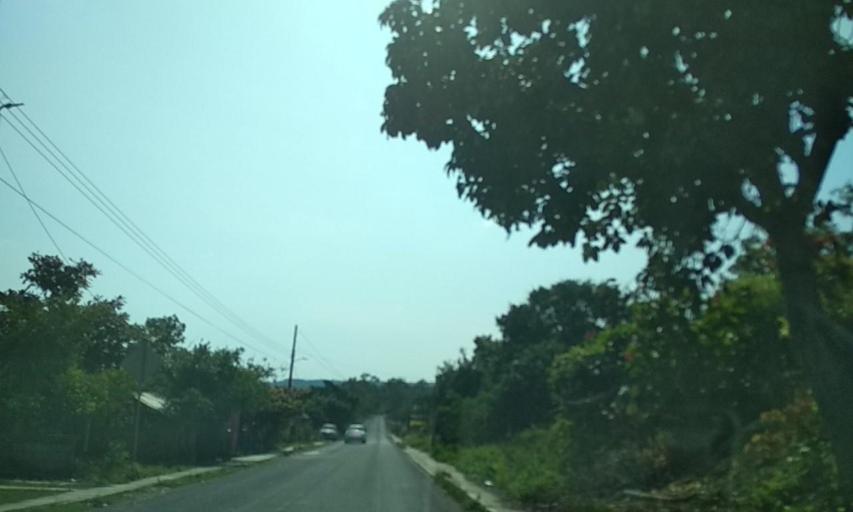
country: MX
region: Veracruz
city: Gutierrez Zamora
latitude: 20.3503
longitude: -97.1510
